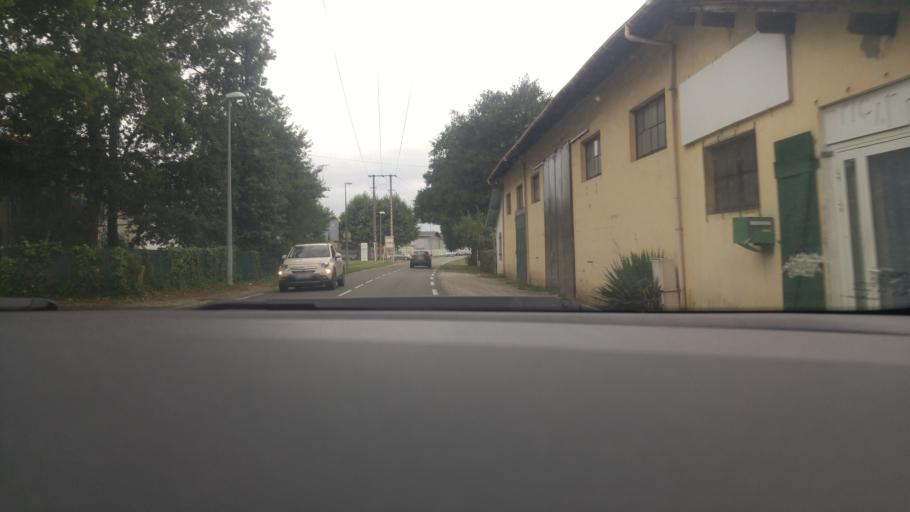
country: FR
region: Aquitaine
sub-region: Departement des Landes
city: Soustons
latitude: 43.7471
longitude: -1.3279
